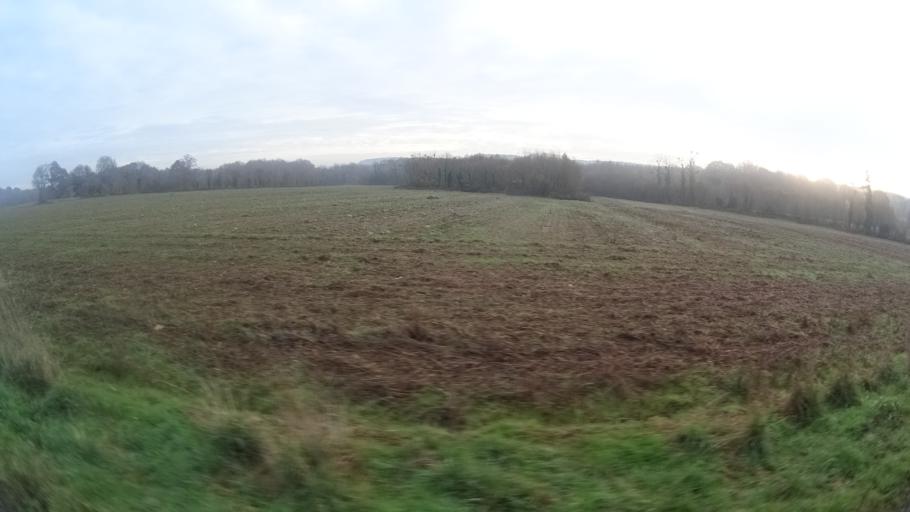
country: FR
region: Pays de la Loire
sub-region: Departement de la Loire-Atlantique
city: Avessac
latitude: 47.6469
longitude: -2.0242
